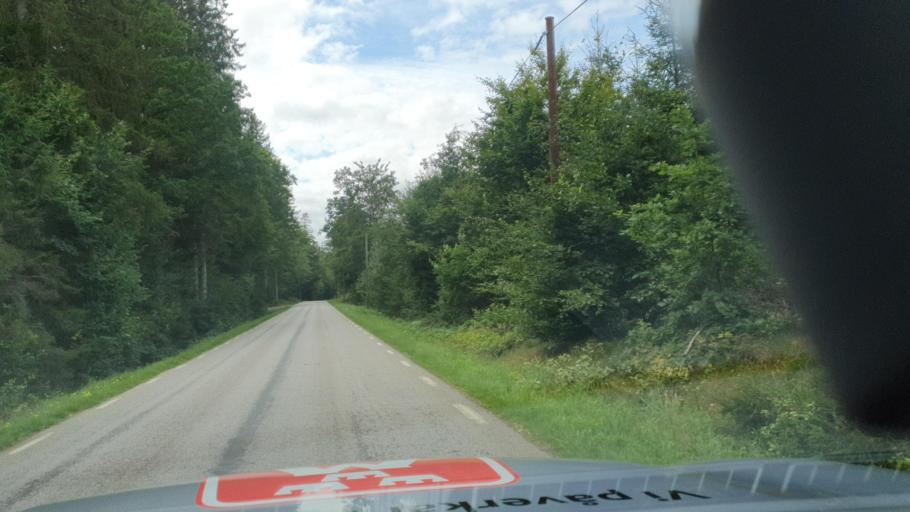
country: SE
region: Blekinge
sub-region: Ronneby Kommun
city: Brakne-Hoby
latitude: 56.3468
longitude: 15.1686
